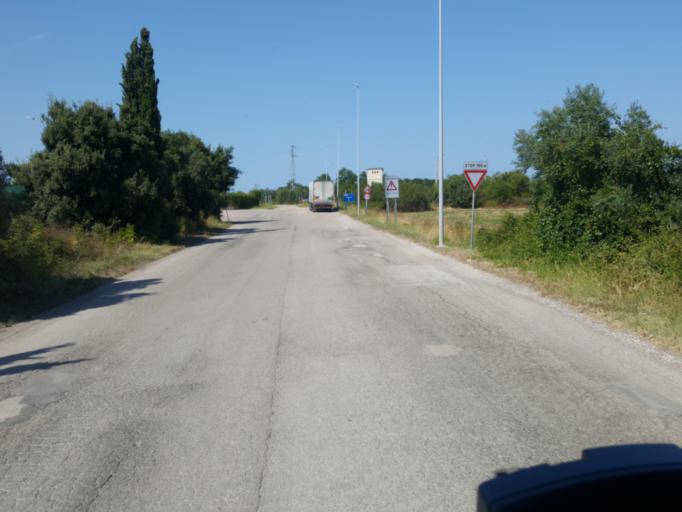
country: IT
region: Abruzzo
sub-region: Provincia di Chieti
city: Salvo Marina
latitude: 42.0646
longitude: 14.7620
